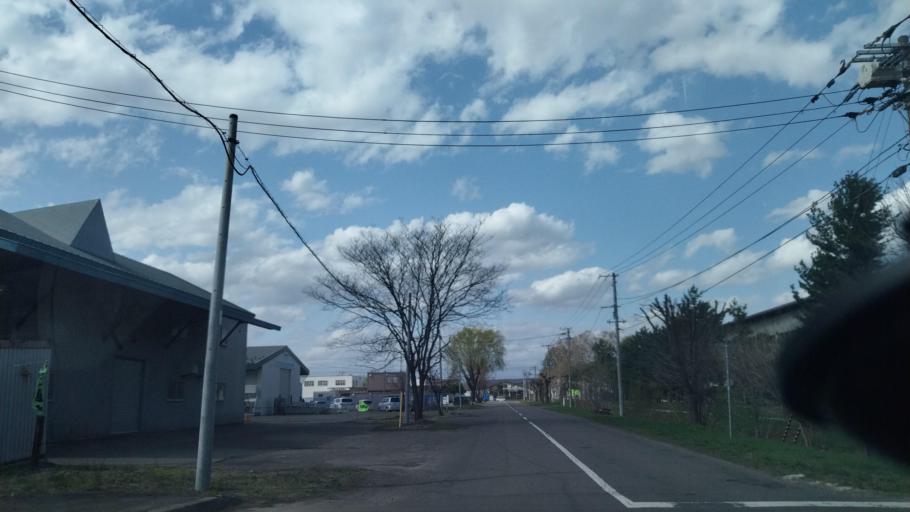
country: JP
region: Hokkaido
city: Obihiro
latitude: 42.9298
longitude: 143.1355
